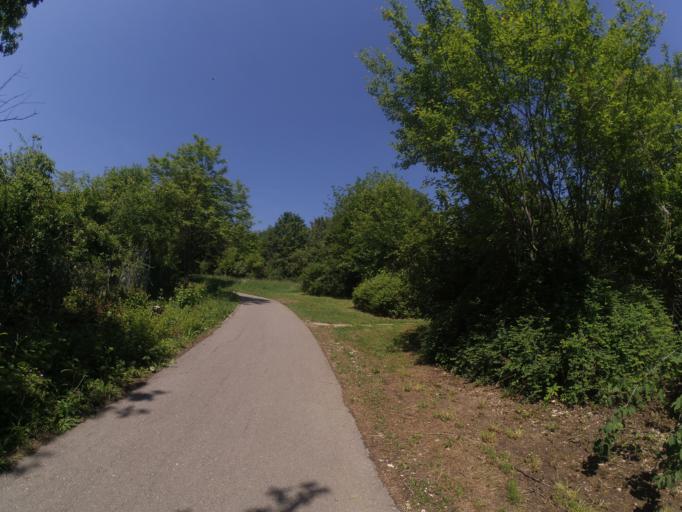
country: DE
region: Baden-Wuerttemberg
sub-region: Tuebingen Region
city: Ulm
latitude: 48.4179
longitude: 9.9675
